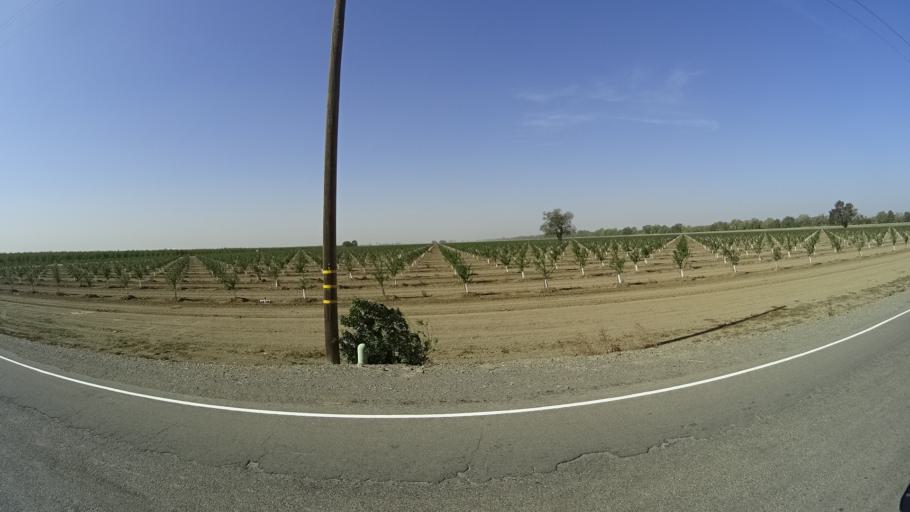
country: US
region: California
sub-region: Yolo County
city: Davis
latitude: 38.5124
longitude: -121.6953
